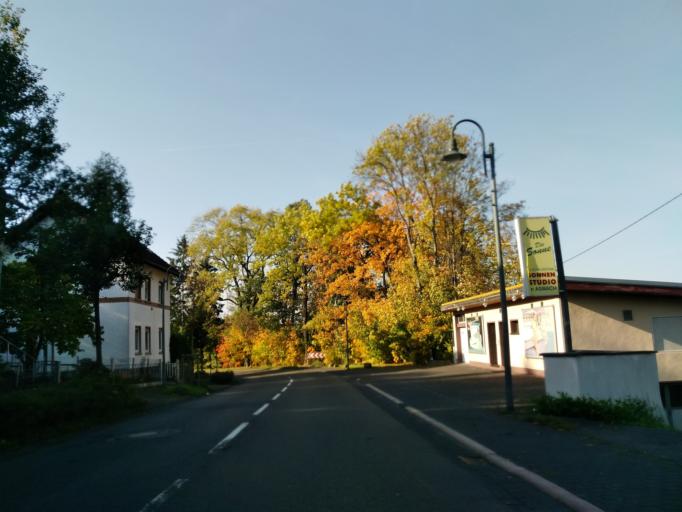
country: DE
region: Rheinland-Pfalz
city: Asbach
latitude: 50.6661
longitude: 7.4222
